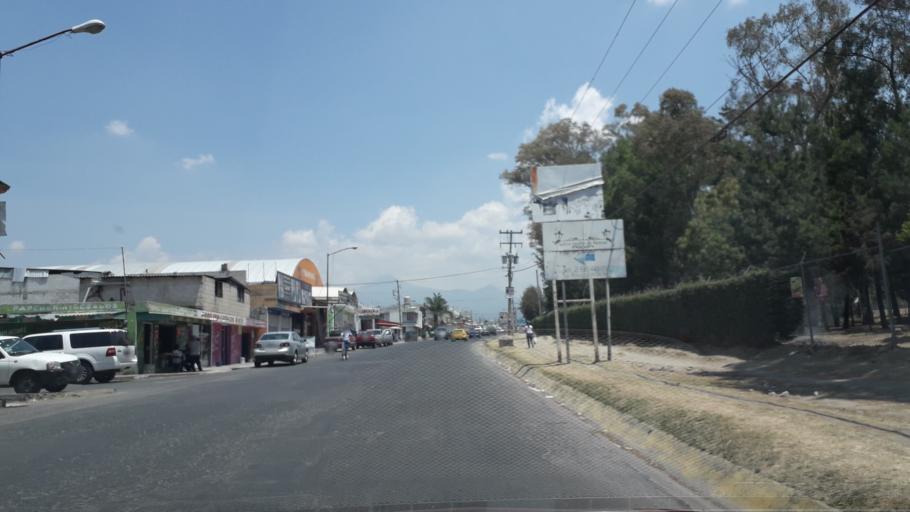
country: MX
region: Puebla
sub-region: Puebla
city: Santa Maria Xonacatepec
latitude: 19.0774
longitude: -98.1118
